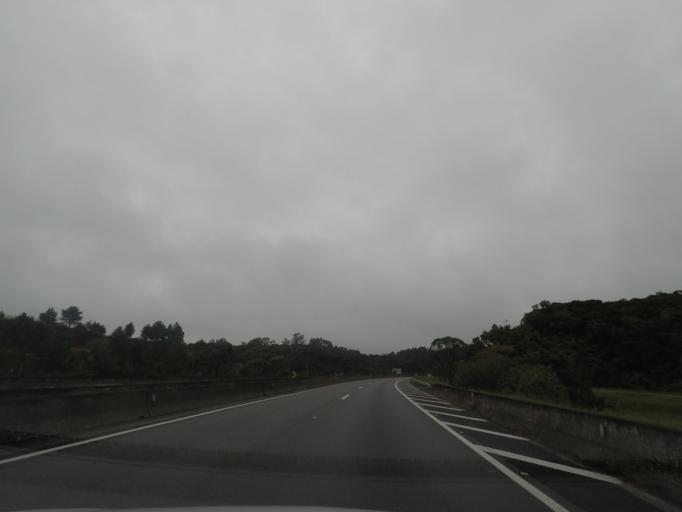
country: BR
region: Parana
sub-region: Campina Grande Do Sul
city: Campina Grande do Sul
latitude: -25.3126
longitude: -49.0164
